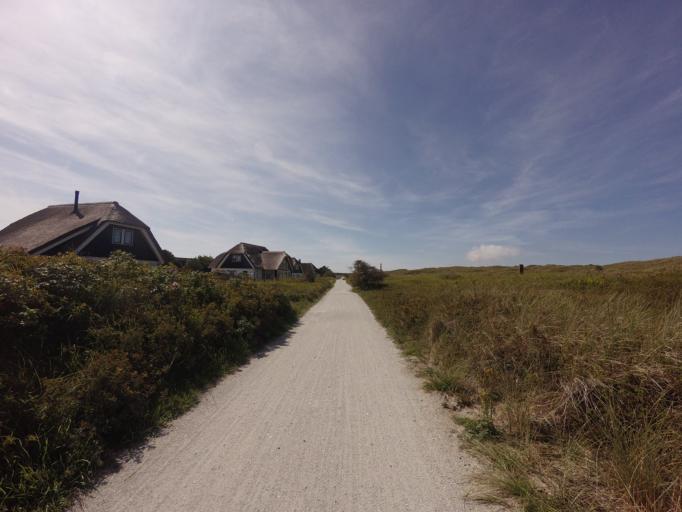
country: NL
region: Friesland
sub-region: Gemeente Ameland
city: Hollum
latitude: 53.4544
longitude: 5.6400
